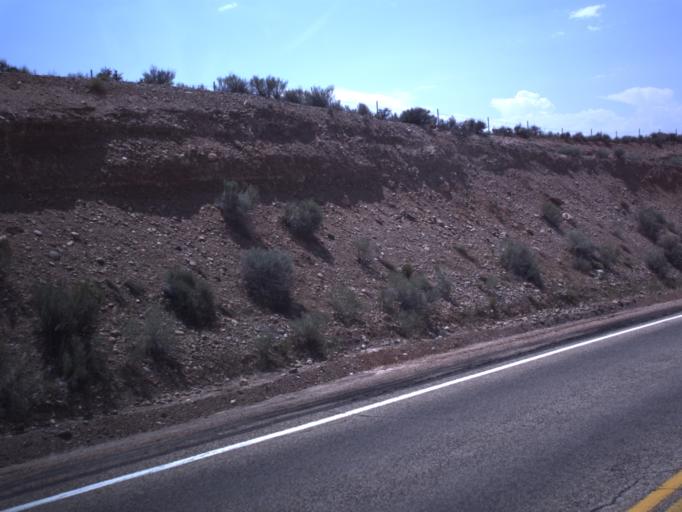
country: US
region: Utah
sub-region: Uintah County
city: Maeser
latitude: 40.4293
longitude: -109.6632
